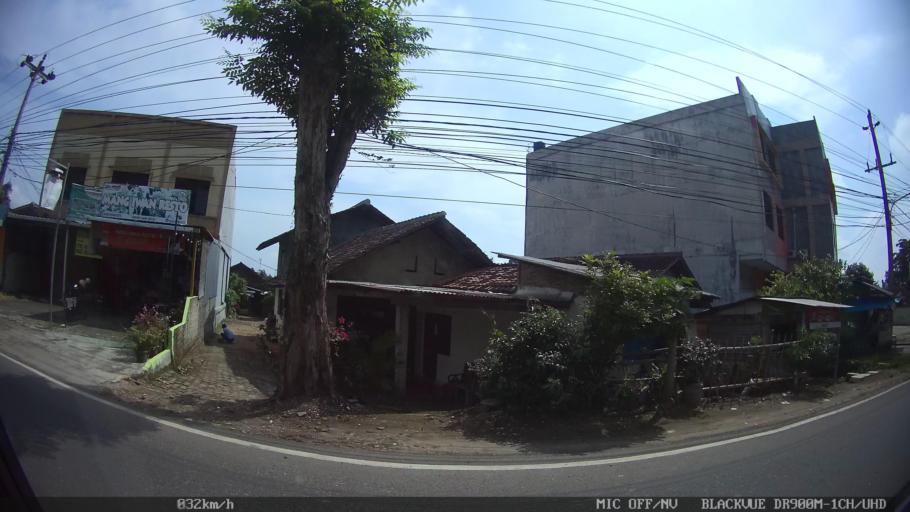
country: ID
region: Lampung
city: Kedaton
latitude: -5.3881
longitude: 105.2696
